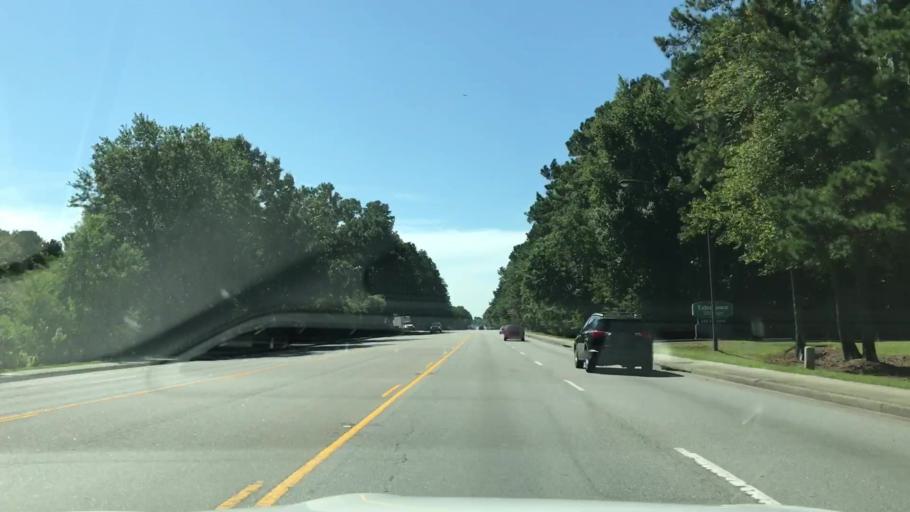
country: US
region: South Carolina
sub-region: Berkeley County
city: Goose Creek
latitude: 33.0223
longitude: -80.0539
